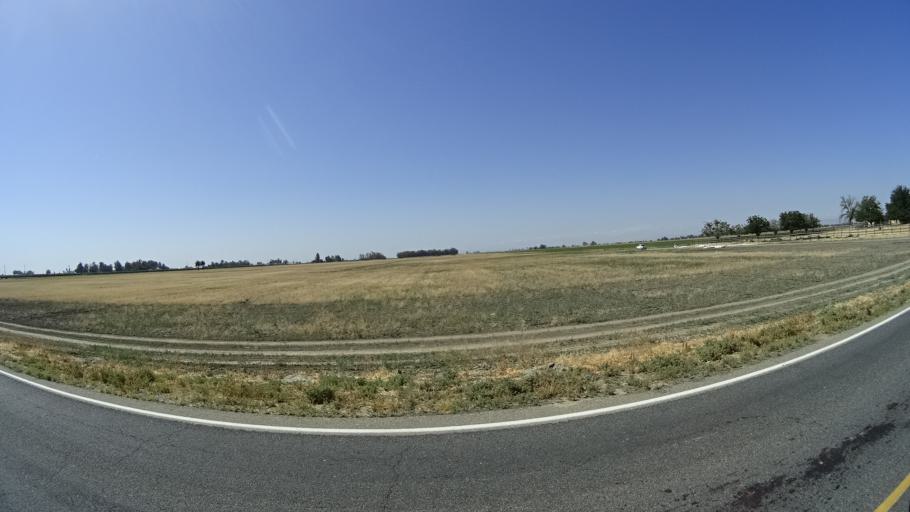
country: US
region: California
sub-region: Kings County
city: Stratford
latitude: 36.2116
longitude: -119.8020
